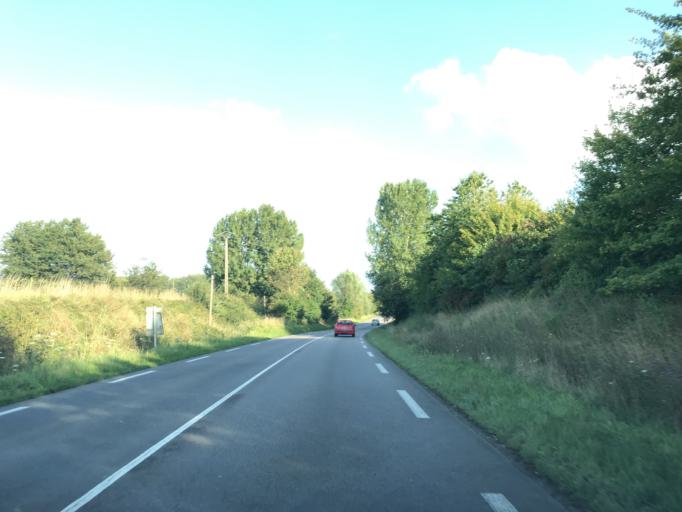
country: FR
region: Haute-Normandie
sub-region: Departement de la Seine-Maritime
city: Bolbec
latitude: 49.5803
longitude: 0.4501
